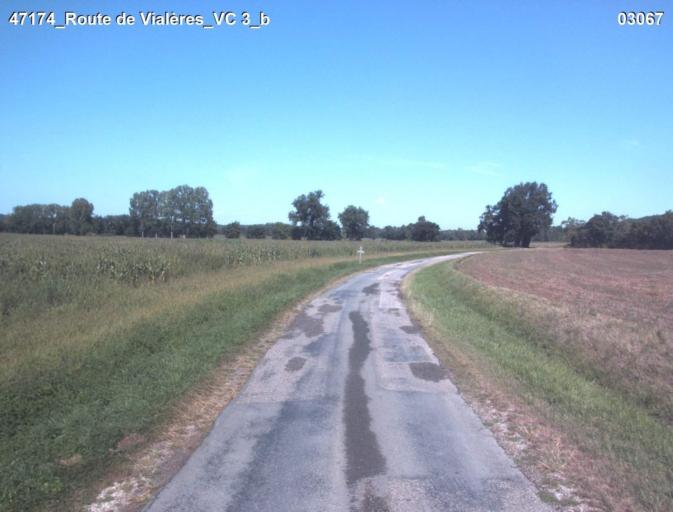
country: FR
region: Aquitaine
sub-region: Departement du Lot-et-Garonne
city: Nerac
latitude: 44.0594
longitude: 0.3857
